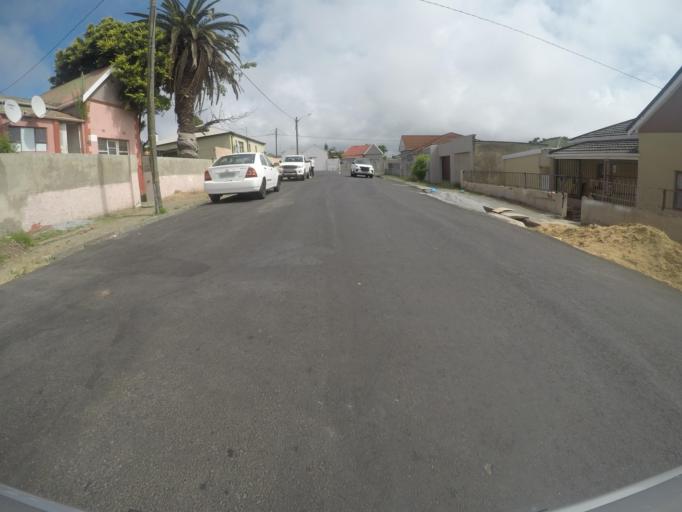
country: ZA
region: Eastern Cape
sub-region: Buffalo City Metropolitan Municipality
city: East London
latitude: -32.9985
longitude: 27.9094
